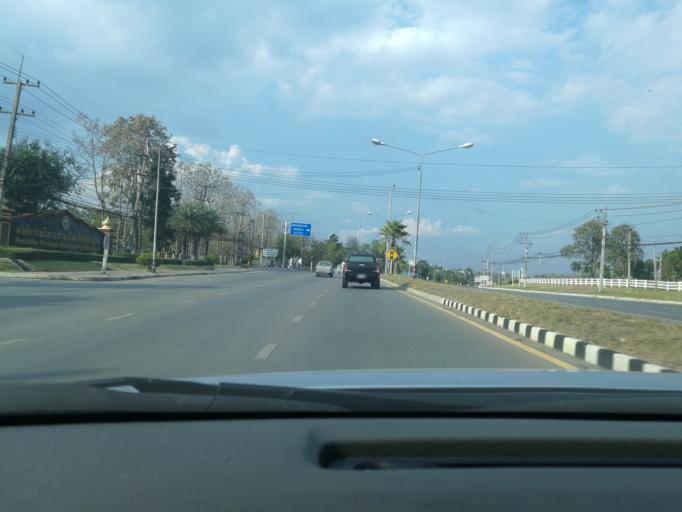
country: TH
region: Phetchabun
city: Phetchabun
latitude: 16.4411
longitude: 101.1514
